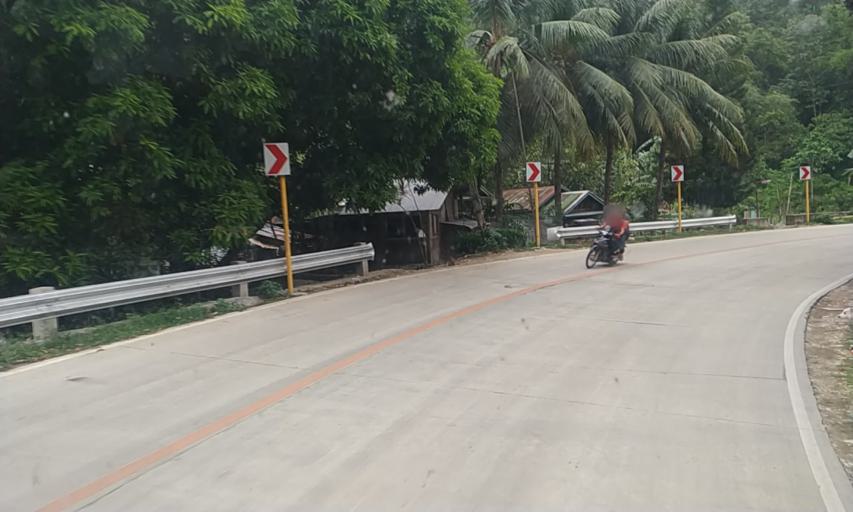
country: PH
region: Central Visayas
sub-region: Province of Negros Oriental
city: Calamba
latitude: 10.1967
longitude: 123.2941
